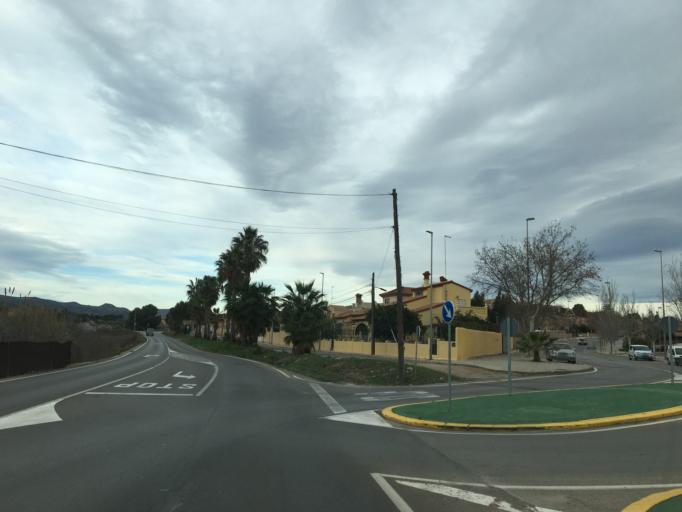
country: ES
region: Murcia
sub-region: Murcia
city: Cartagena
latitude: 37.6128
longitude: -1.0198
